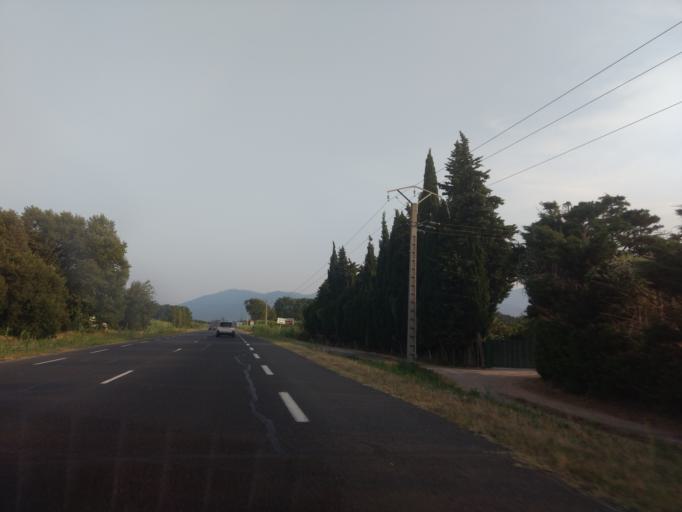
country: FR
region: Languedoc-Roussillon
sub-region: Departement des Pyrenees-Orientales
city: Latour-Bas-Elne
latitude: 42.6013
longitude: 3.0242
